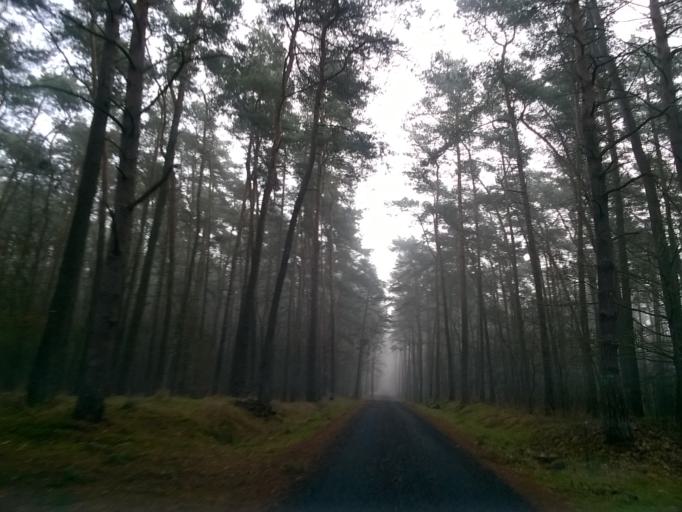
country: PL
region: Kujawsko-Pomorskie
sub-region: Powiat nakielski
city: Kcynia
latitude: 53.0508
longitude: 17.4688
